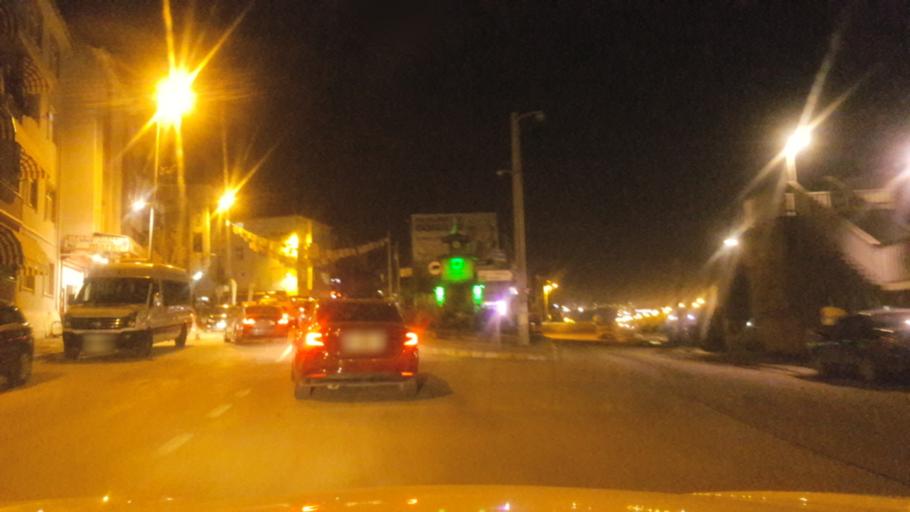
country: TR
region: Kocaeli
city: Tavsanli
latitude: 40.7881
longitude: 29.5330
